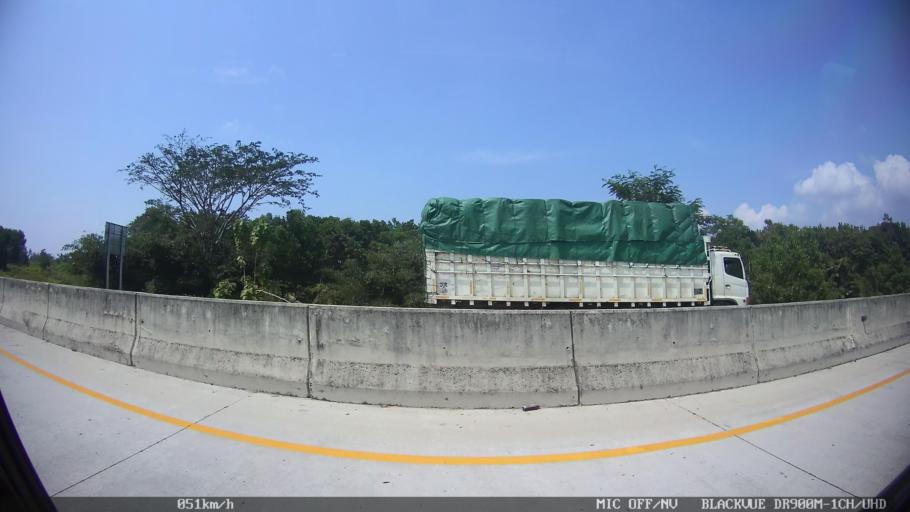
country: ID
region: Lampung
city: Kedaton
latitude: -5.3219
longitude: 105.2729
